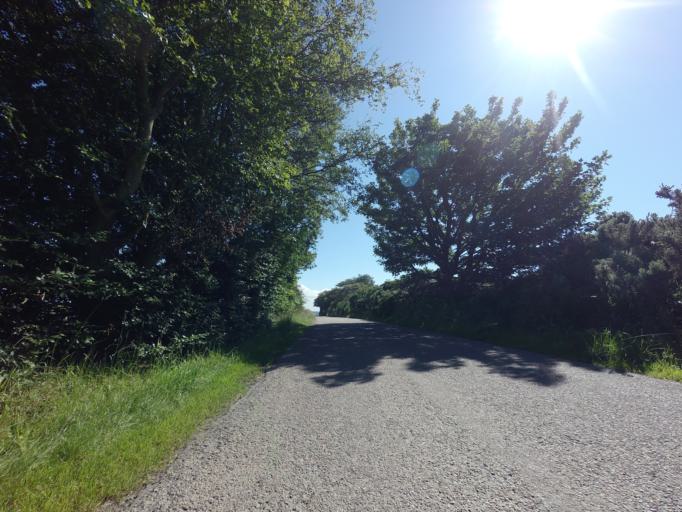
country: GB
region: Scotland
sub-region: Aberdeenshire
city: Macduff
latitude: 57.6495
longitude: -2.5042
